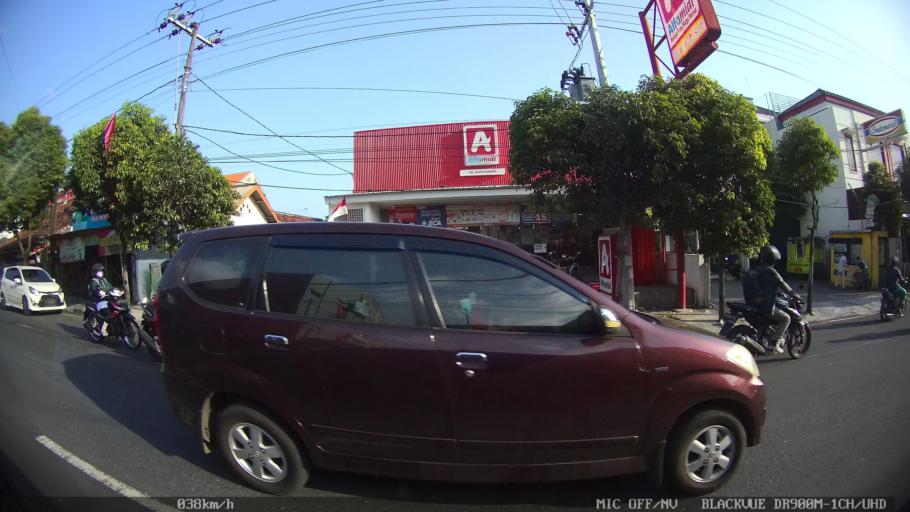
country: ID
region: Daerah Istimewa Yogyakarta
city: Yogyakarta
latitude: -7.8012
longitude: 110.3494
